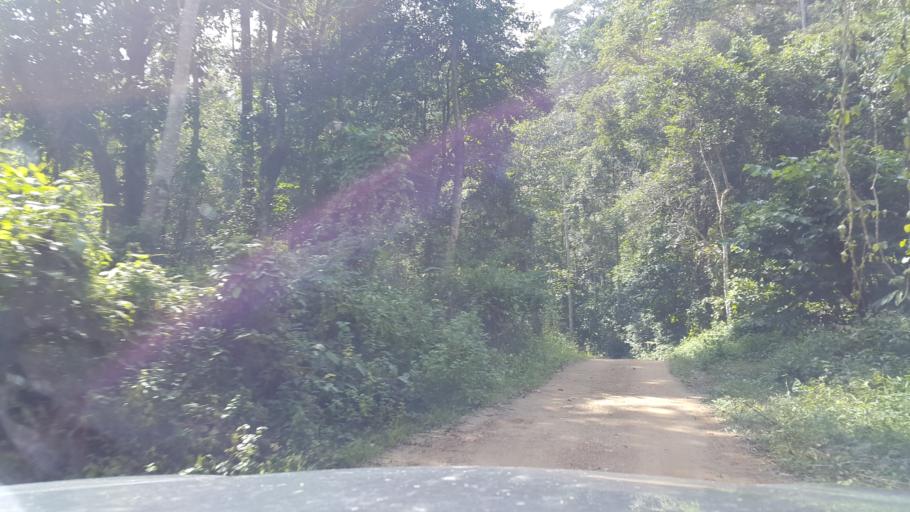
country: TH
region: Chiang Mai
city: Phrao
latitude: 19.1059
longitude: 99.2737
